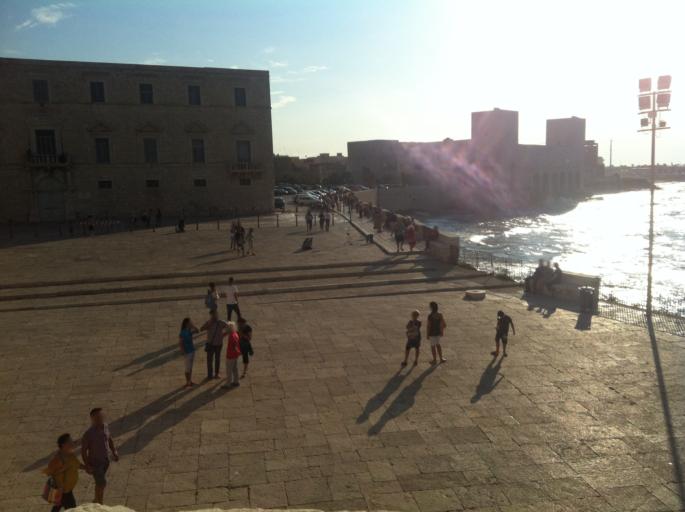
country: IT
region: Apulia
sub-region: Provincia di Barletta - Andria - Trani
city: Trani
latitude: 41.2823
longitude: 16.4182
